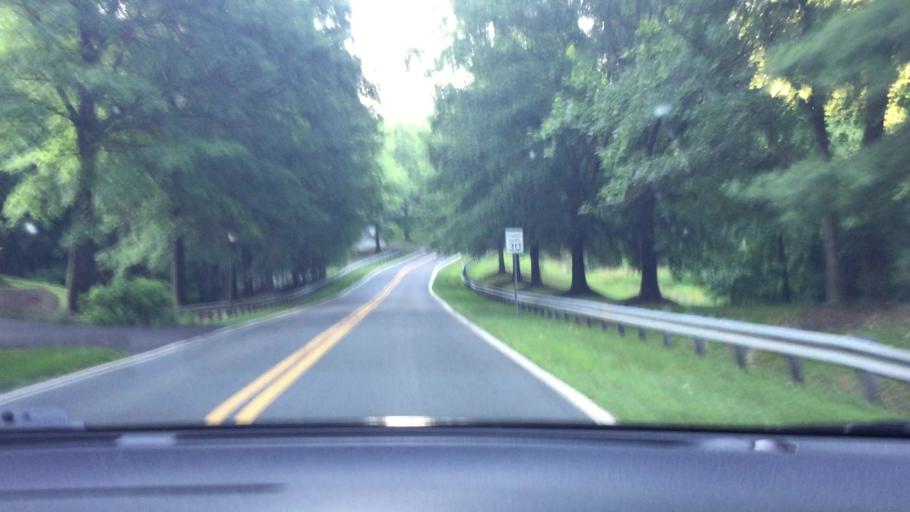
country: US
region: Maryland
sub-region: Montgomery County
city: Potomac
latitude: 39.0141
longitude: -77.1885
